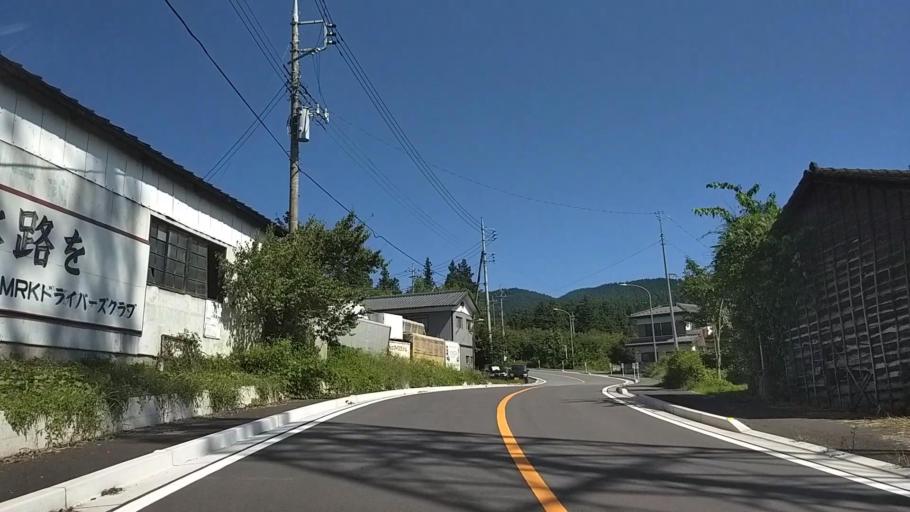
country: JP
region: Gunma
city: Annaka
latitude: 36.3391
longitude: 138.7268
